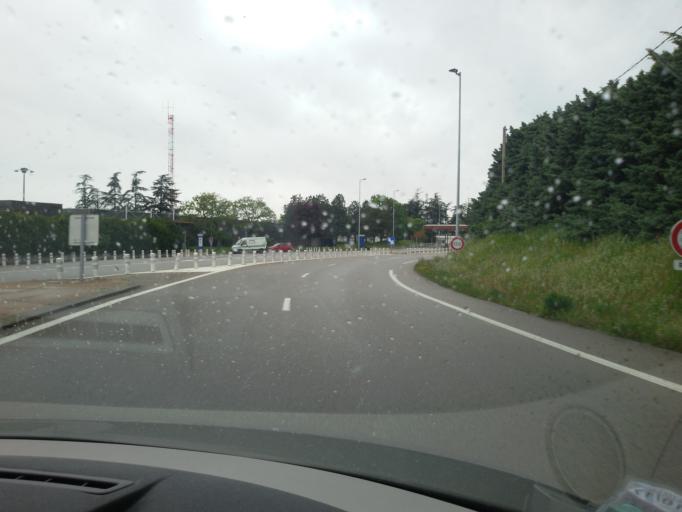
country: FR
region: Rhone-Alpes
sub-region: Departement de la Drome
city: Bourg-les-Valence
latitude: 44.9686
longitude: 4.8874
